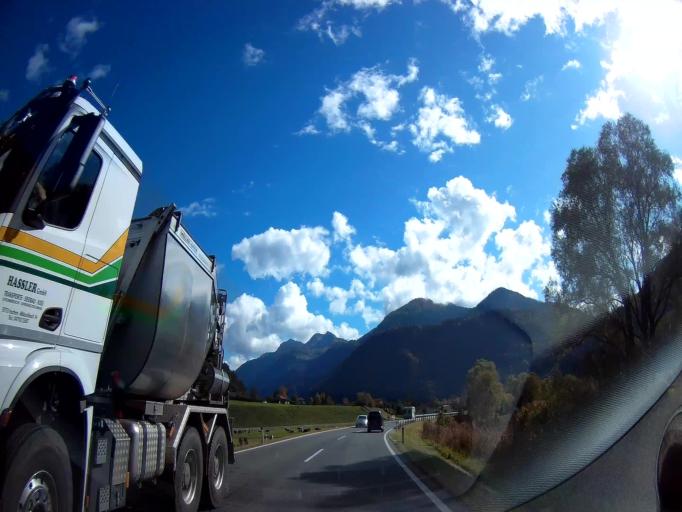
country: AT
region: Carinthia
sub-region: Politischer Bezirk Spittal an der Drau
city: Oberdrauburg
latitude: 46.7529
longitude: 12.9599
